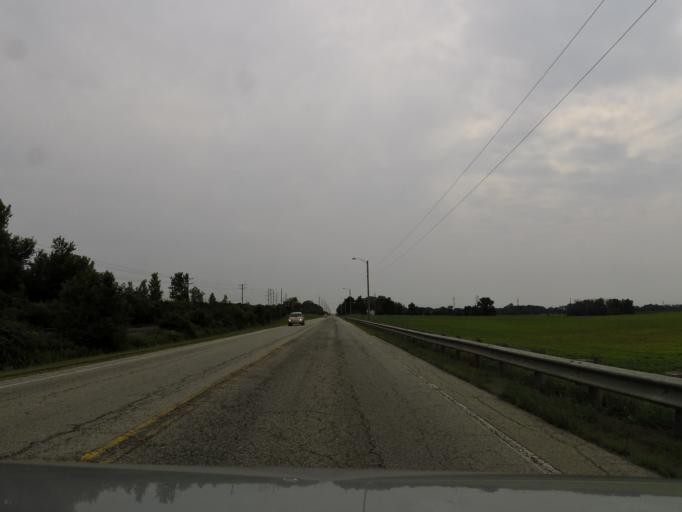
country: US
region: Ohio
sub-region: Clinton County
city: Wilmington
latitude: 39.4243
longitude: -83.8365
